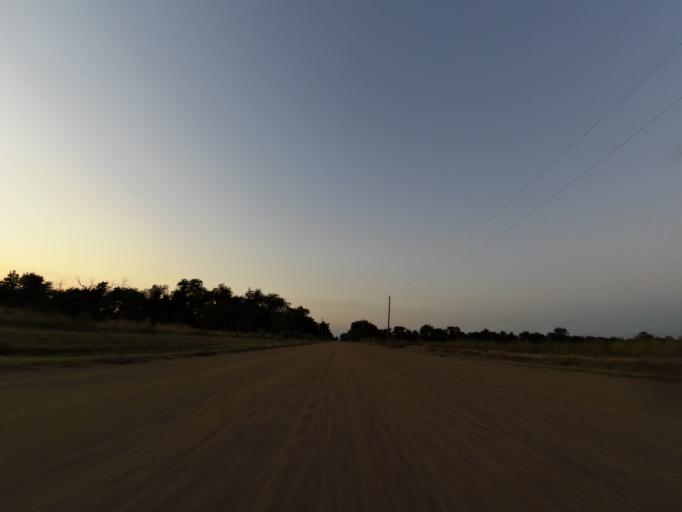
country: US
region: Kansas
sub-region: Reno County
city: South Hutchinson
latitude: 37.9783
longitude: -98.0319
